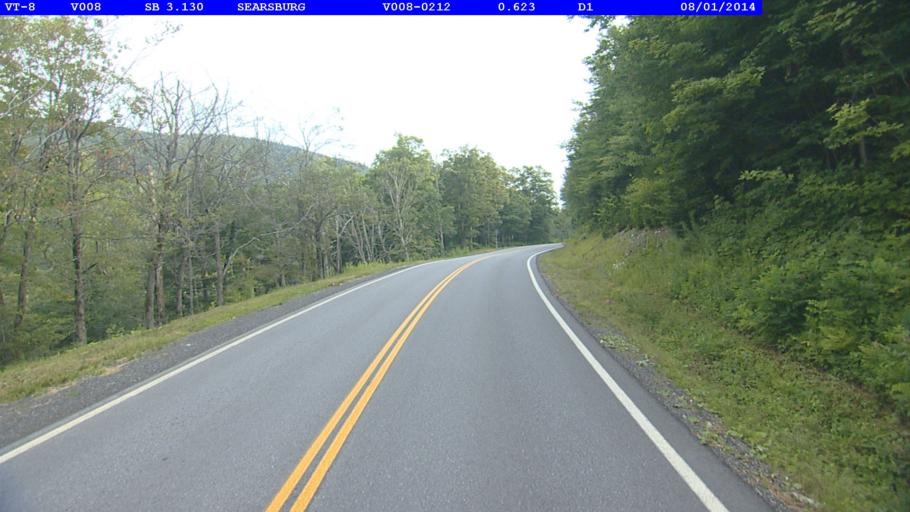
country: US
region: Vermont
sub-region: Windham County
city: Dover
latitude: 42.8664
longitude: -72.9708
